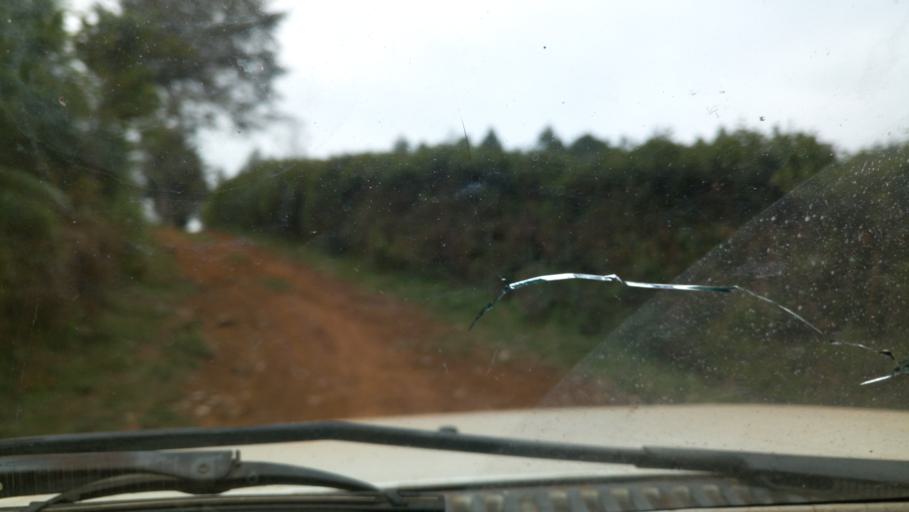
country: KE
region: Murang'a District
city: Kangema
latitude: -0.7590
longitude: 36.8387
